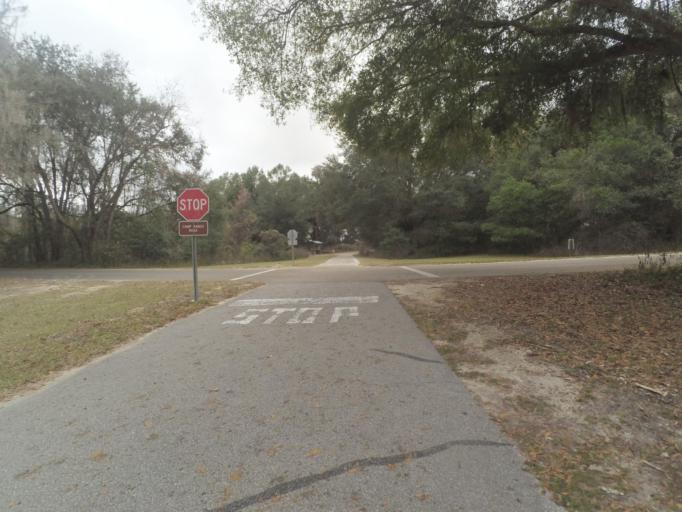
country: US
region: Florida
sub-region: Alachua County
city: Gainesville
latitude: 29.6098
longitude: -82.3036
